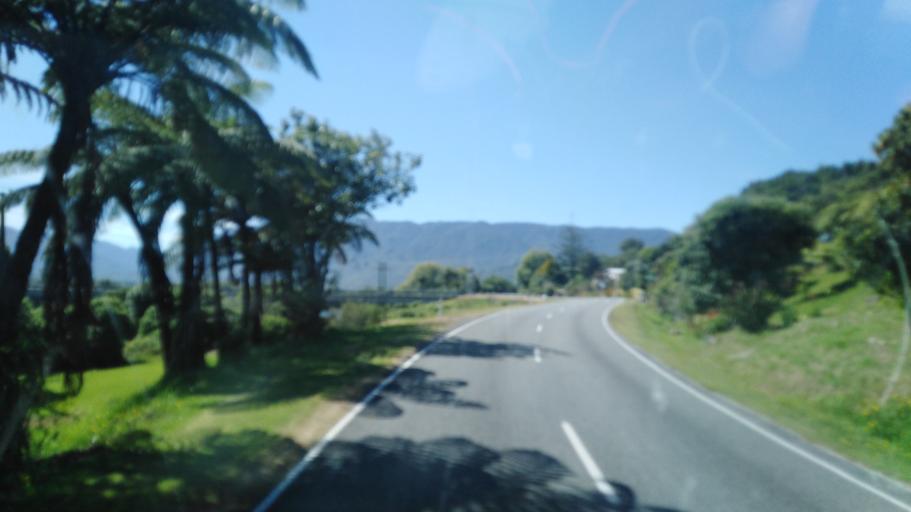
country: NZ
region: West Coast
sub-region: Buller District
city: Westport
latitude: -41.2611
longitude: 172.1292
